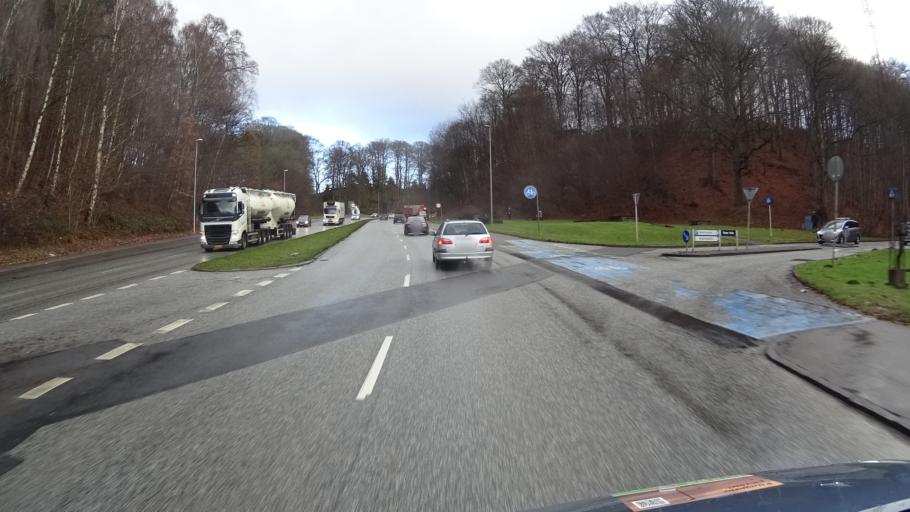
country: DK
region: South Denmark
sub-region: Vejle Kommune
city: Vejle
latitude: 55.7148
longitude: 9.5489
